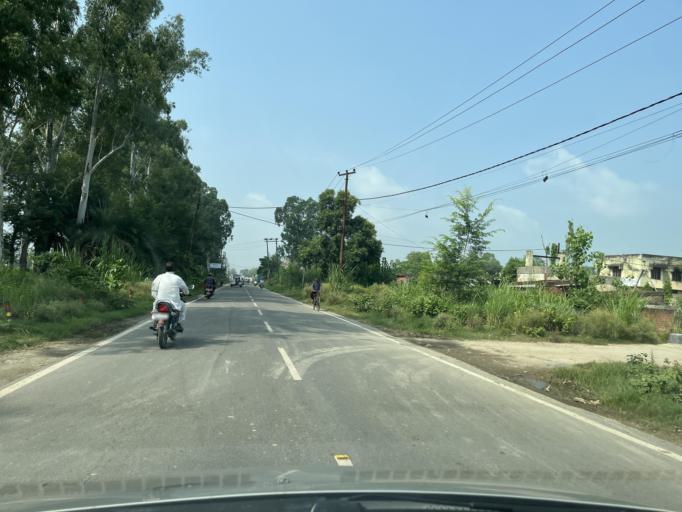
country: IN
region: Uttarakhand
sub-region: Udham Singh Nagar
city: Bazpur
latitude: 29.1674
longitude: 79.1618
